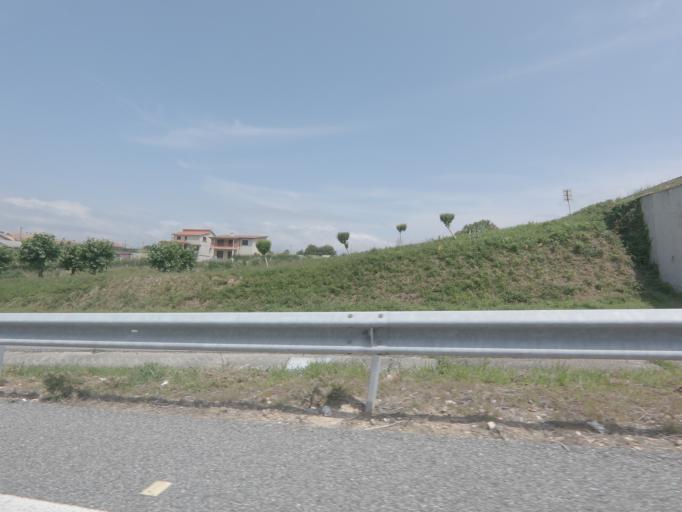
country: ES
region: Galicia
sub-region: Provincia de Pontevedra
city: Baiona
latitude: 42.1004
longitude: -8.8248
